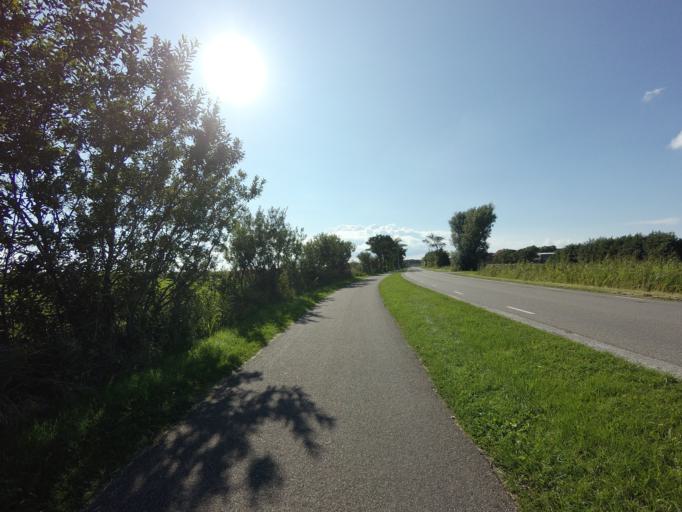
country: NL
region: Friesland
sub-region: Gemeente Terschelling
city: West-Terschelling
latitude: 53.3752
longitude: 5.2584
